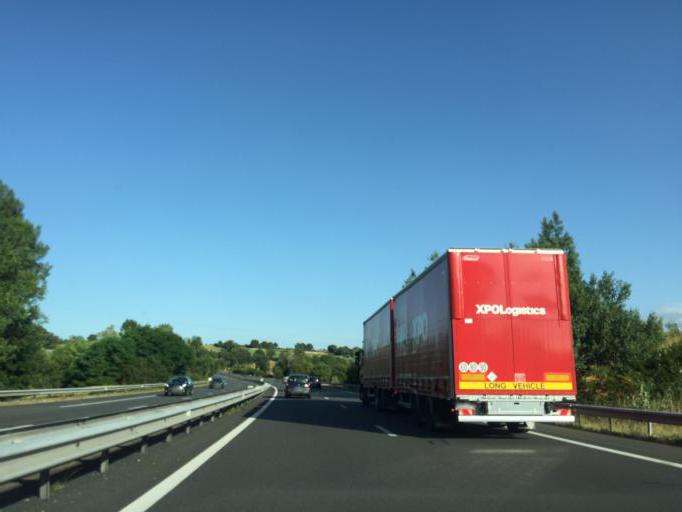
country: FR
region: Auvergne
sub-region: Departement de l'Allier
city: Montmarault
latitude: 46.3329
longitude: 2.8923
